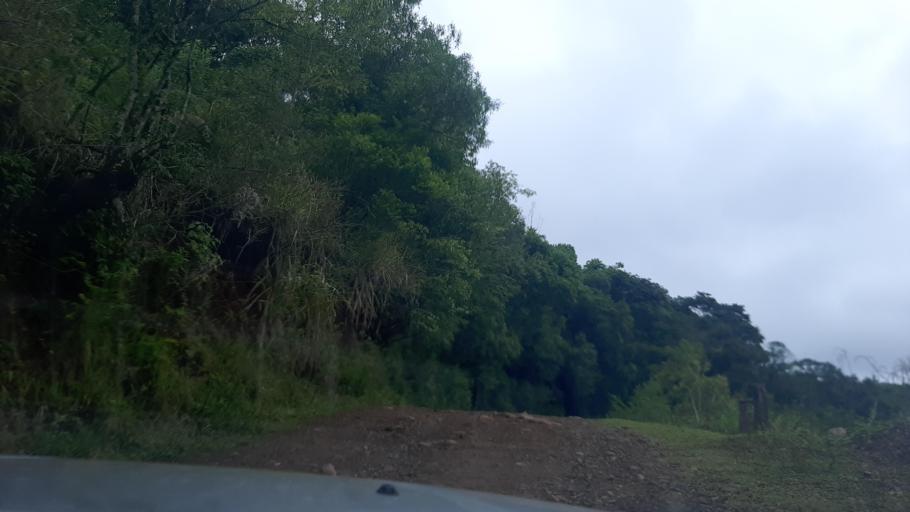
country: BR
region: Parana
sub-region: Ampere
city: Ampere
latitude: -26.0581
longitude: -53.5481
